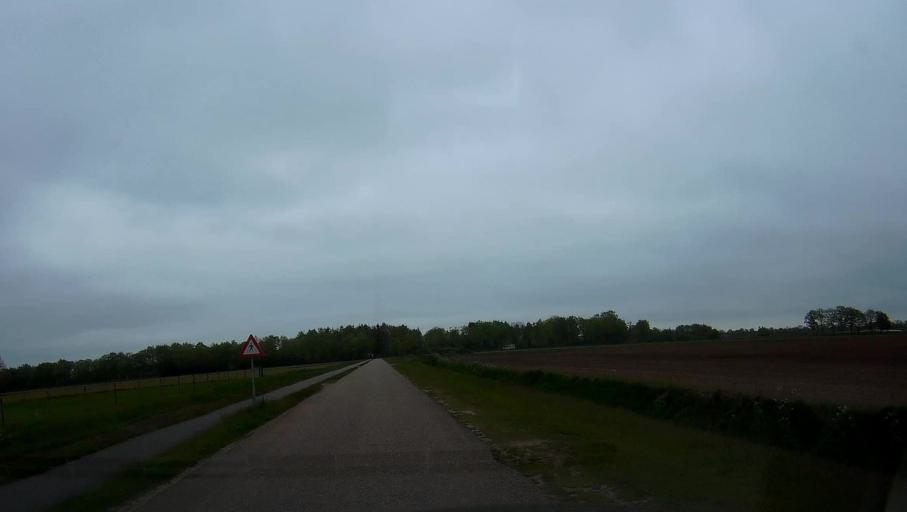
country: NL
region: Drenthe
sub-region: Gemeente Borger-Odoorn
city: Borger
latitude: 52.9708
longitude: 6.7717
